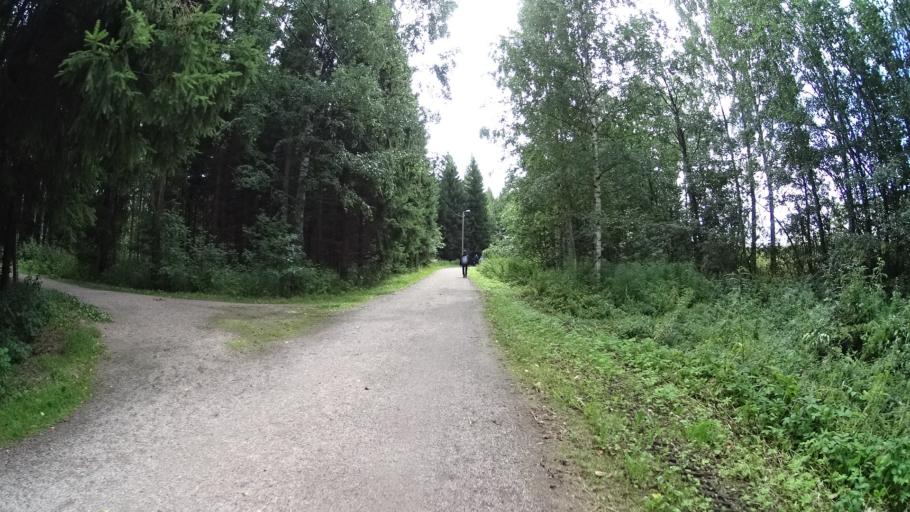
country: FI
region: Uusimaa
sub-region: Helsinki
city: Teekkarikylae
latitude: 60.2655
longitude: 24.8996
